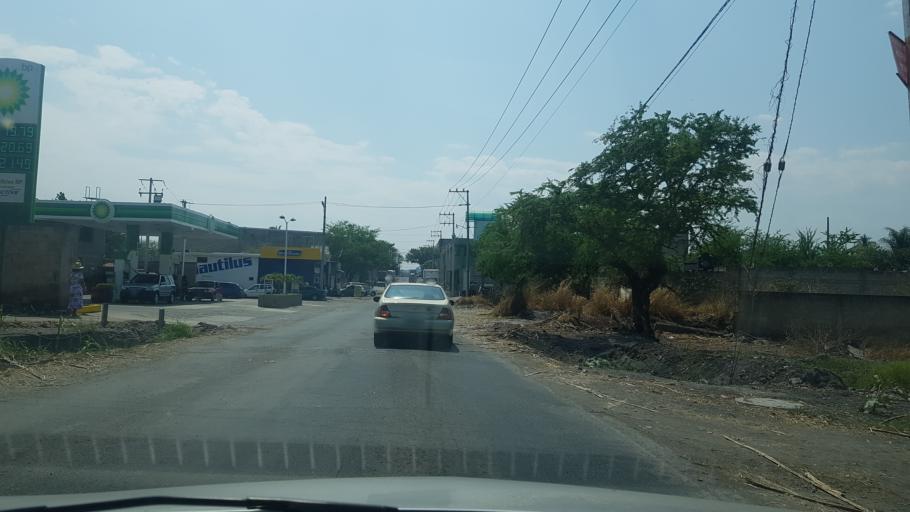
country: MX
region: Morelos
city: Zacatepec
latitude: 18.6587
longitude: -99.1840
